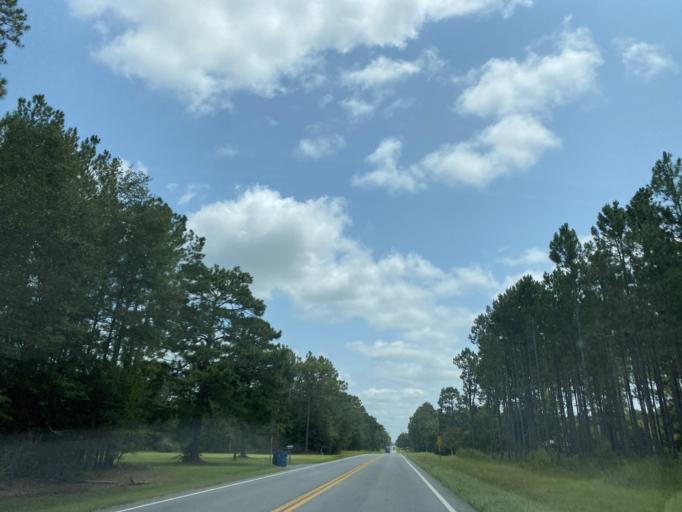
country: US
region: Georgia
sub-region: Bacon County
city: Alma
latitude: 31.6966
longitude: -82.5091
